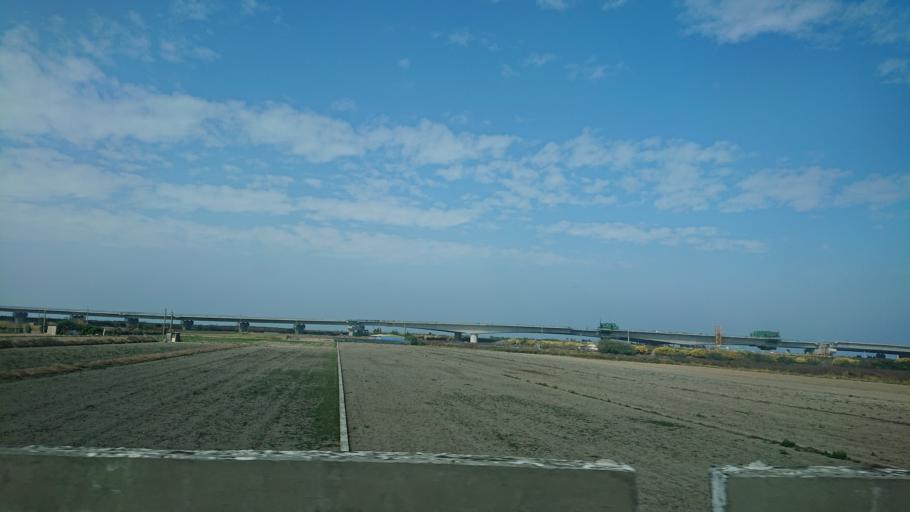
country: TW
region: Taiwan
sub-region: Changhua
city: Chang-hua
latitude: 23.9329
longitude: 120.3223
